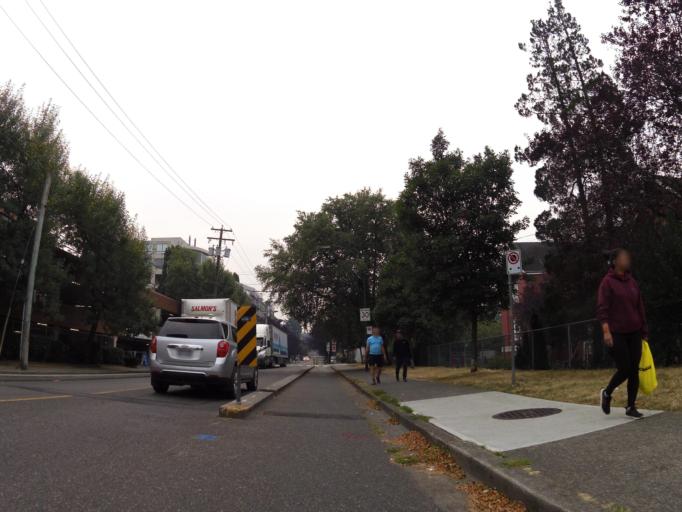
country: CA
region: British Columbia
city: West End
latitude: 49.2723
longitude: -123.1479
